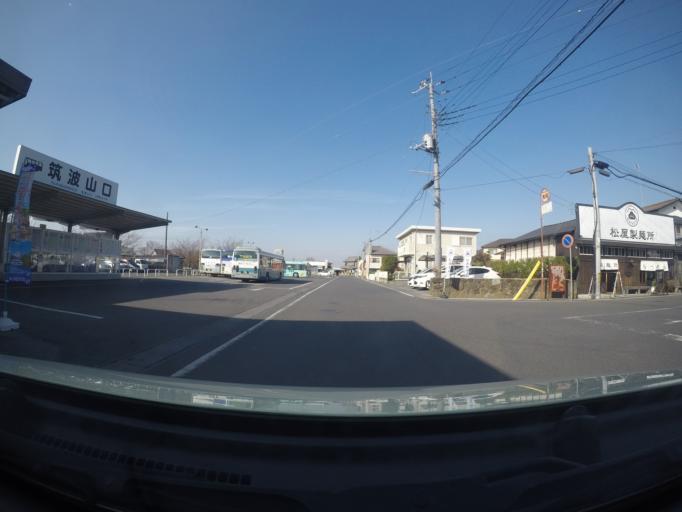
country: JP
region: Ibaraki
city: Tsukuba
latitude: 36.2070
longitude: 140.0803
